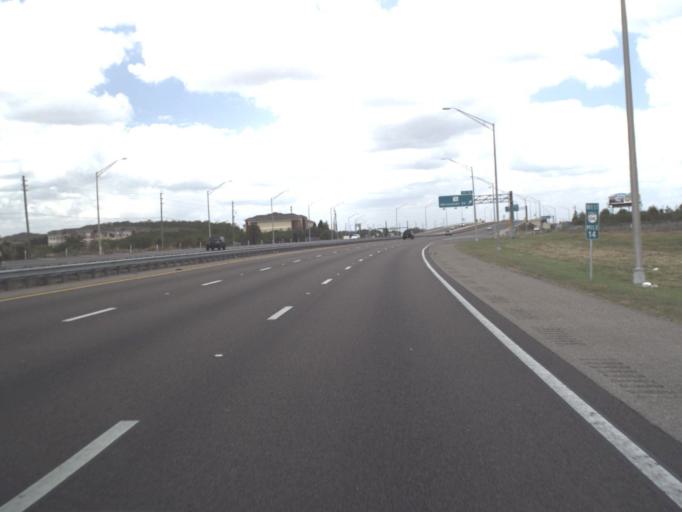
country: US
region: Florida
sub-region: Orange County
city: Conway
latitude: 28.4490
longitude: -81.2567
